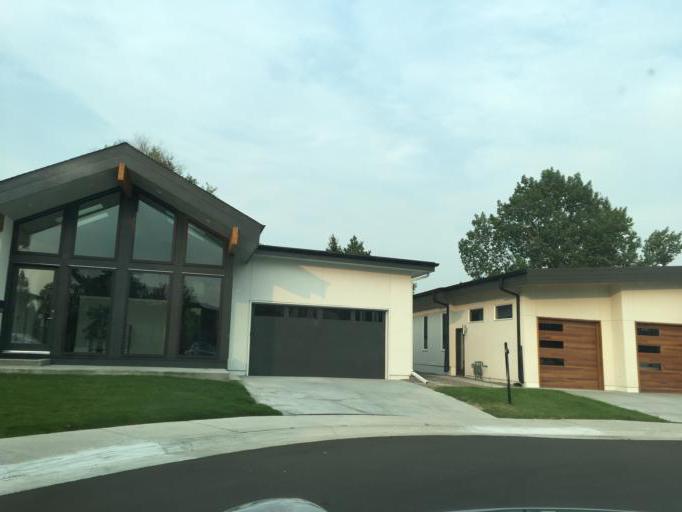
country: US
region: Colorado
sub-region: Arapahoe County
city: Glendale
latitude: 39.6831
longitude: -104.9251
